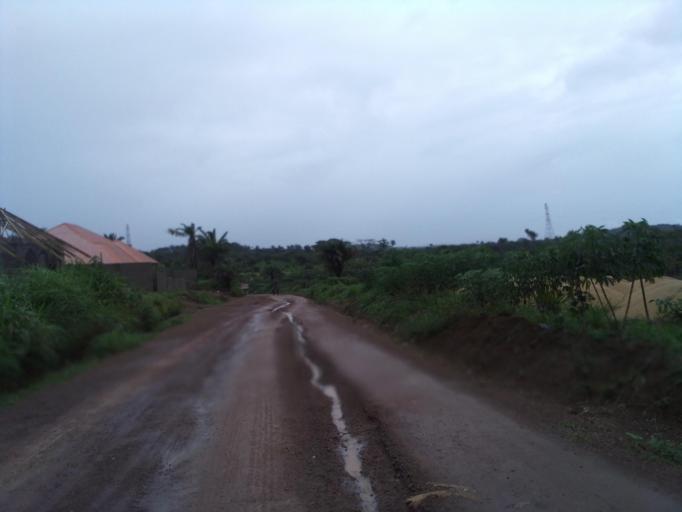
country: SL
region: Eastern Province
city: Kenema
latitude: 7.8757
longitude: -11.1529
